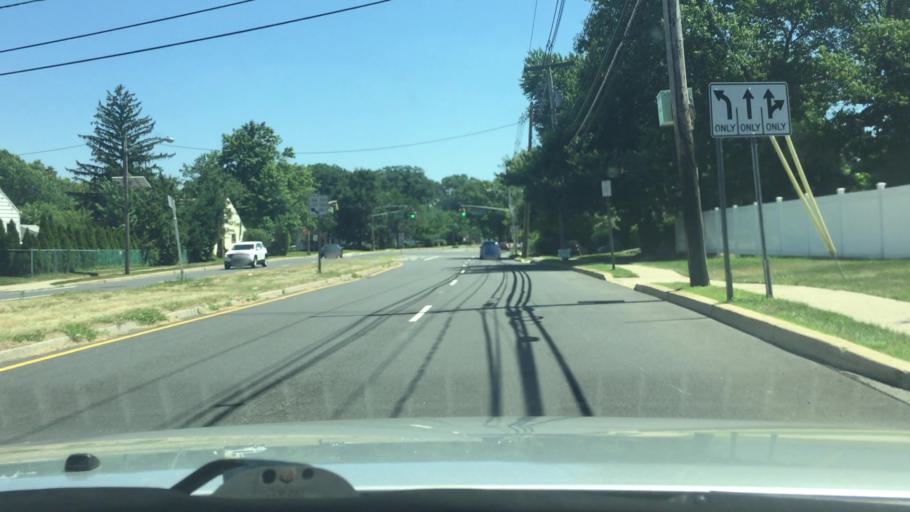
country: US
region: New Jersey
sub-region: Middlesex County
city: South River
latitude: 40.4287
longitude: -74.3917
